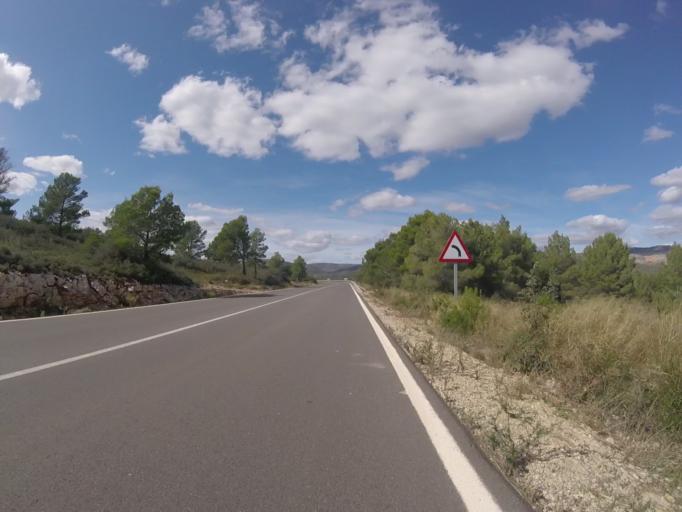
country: ES
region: Valencia
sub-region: Provincia de Castello
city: Chert/Xert
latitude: 40.4399
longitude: 0.1109
